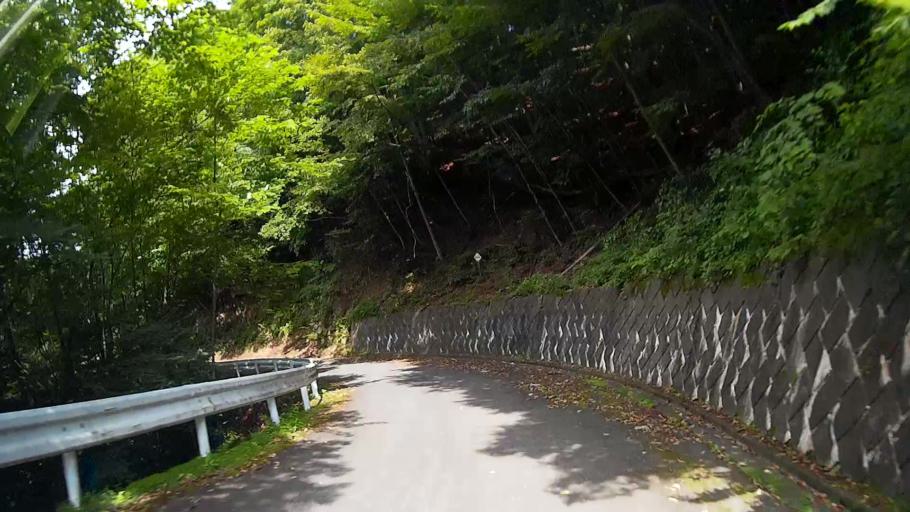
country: JP
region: Saitama
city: Chichibu
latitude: 35.8913
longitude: 139.1109
